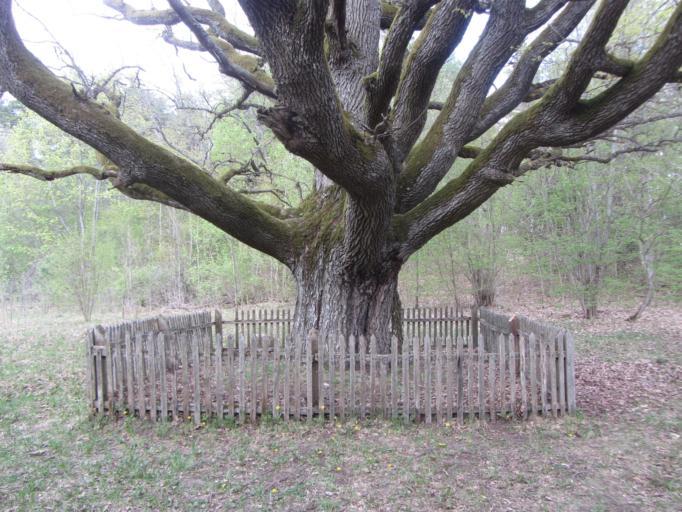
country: LT
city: Salcininkai
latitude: 54.2903
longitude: 25.5529
